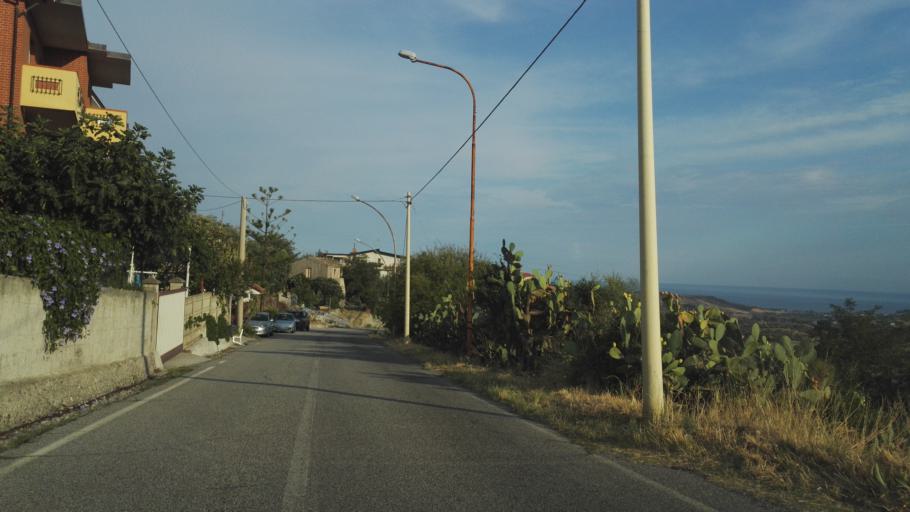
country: IT
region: Calabria
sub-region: Provincia di Reggio Calabria
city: Stignano
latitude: 38.4097
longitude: 16.4709
